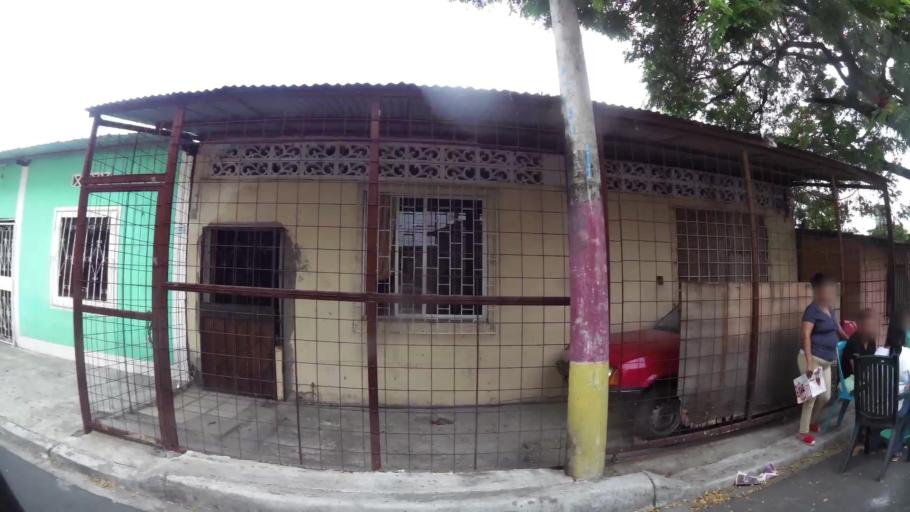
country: EC
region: Guayas
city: Guayaquil
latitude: -2.2383
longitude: -79.9078
